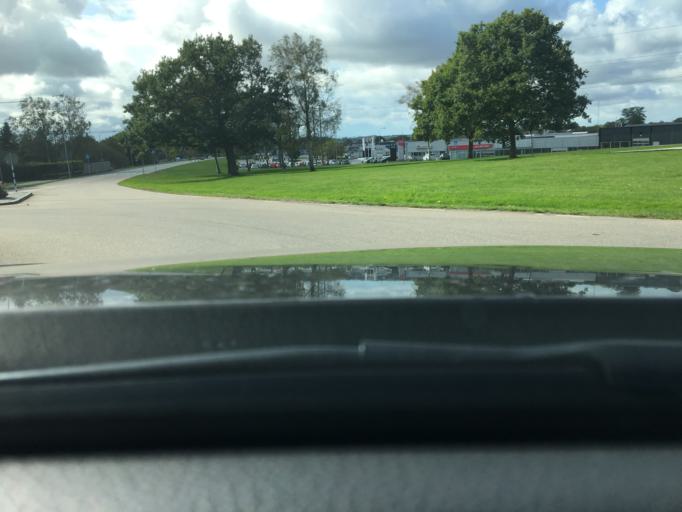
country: SE
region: Skane
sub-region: Horby Kommun
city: Hoerby
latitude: 55.8572
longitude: 13.6749
